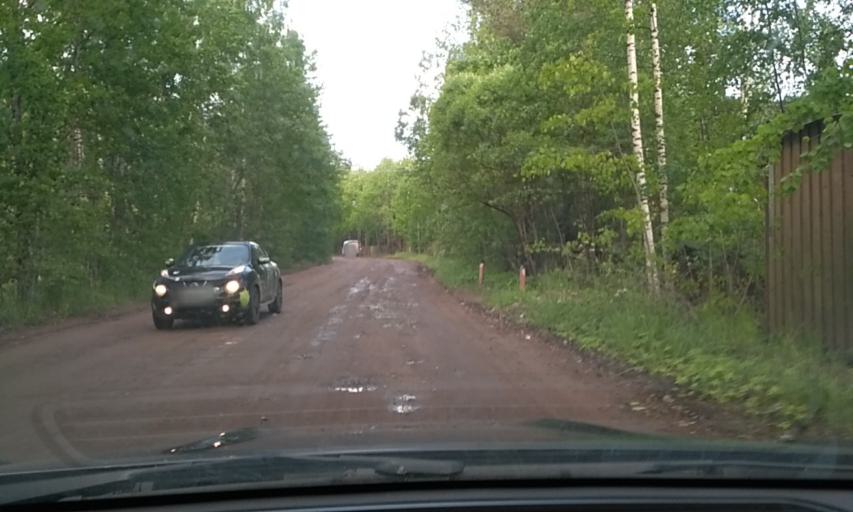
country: RU
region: Leningrad
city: Otradnoye
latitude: 59.7871
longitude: 30.7820
